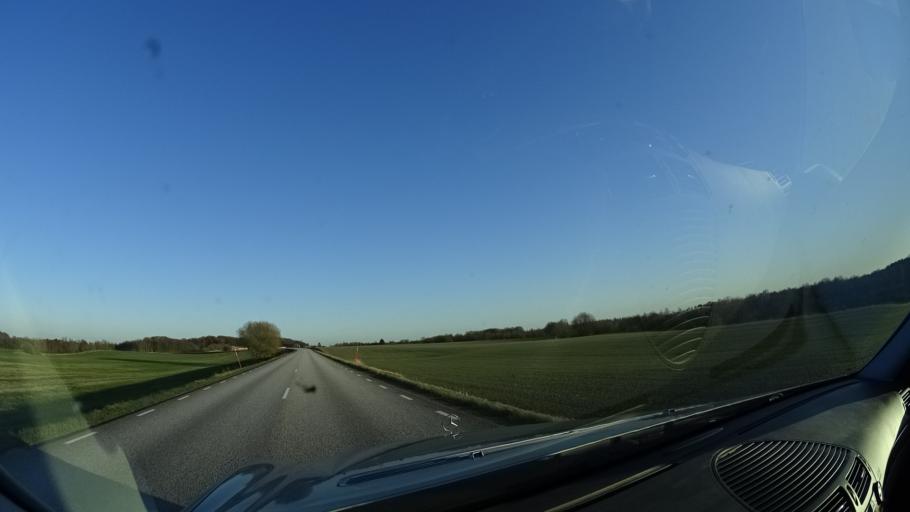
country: SE
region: Skane
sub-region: Klippans Kommun
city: Ljungbyhed
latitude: 55.9743
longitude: 13.2031
